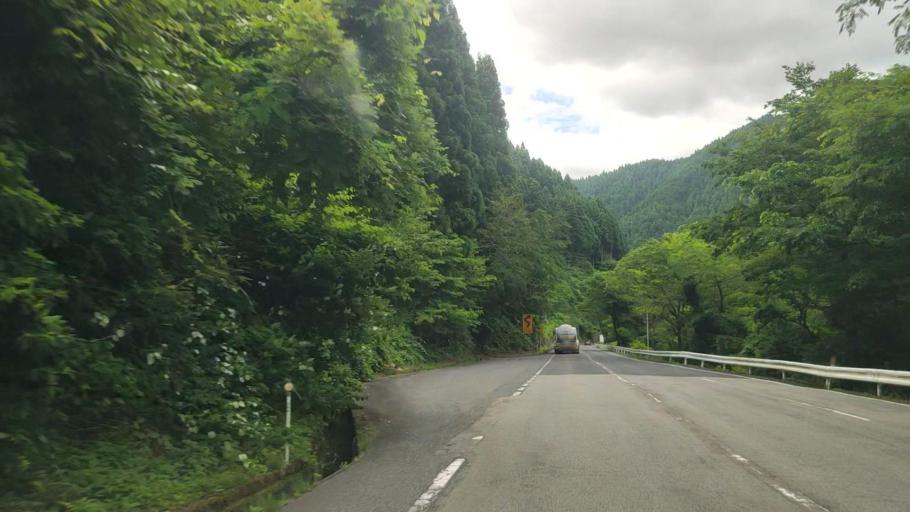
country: JP
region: Tottori
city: Yonago
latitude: 35.2591
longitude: 133.4377
